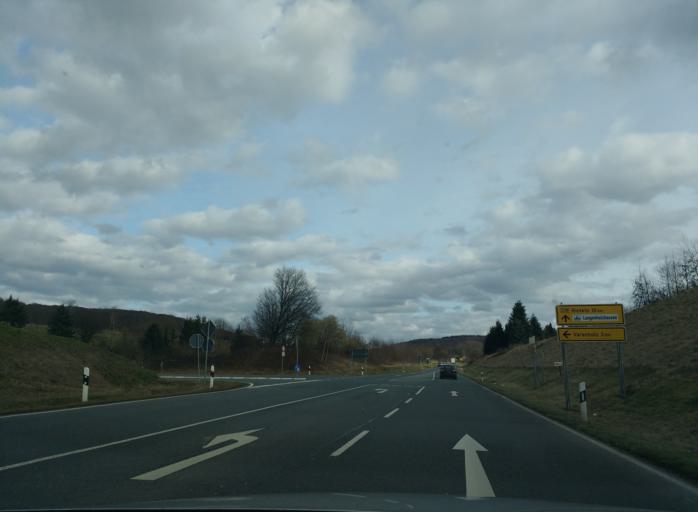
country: DE
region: North Rhine-Westphalia
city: Porta Westfalica
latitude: 52.1533
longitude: 8.9687
